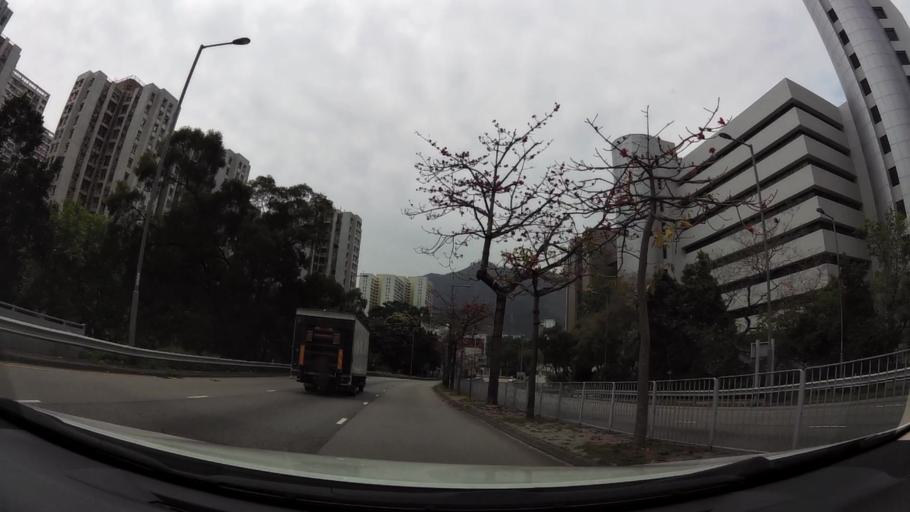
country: HK
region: Tuen Mun
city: Tuen Mun
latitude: 22.3900
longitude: 113.9769
